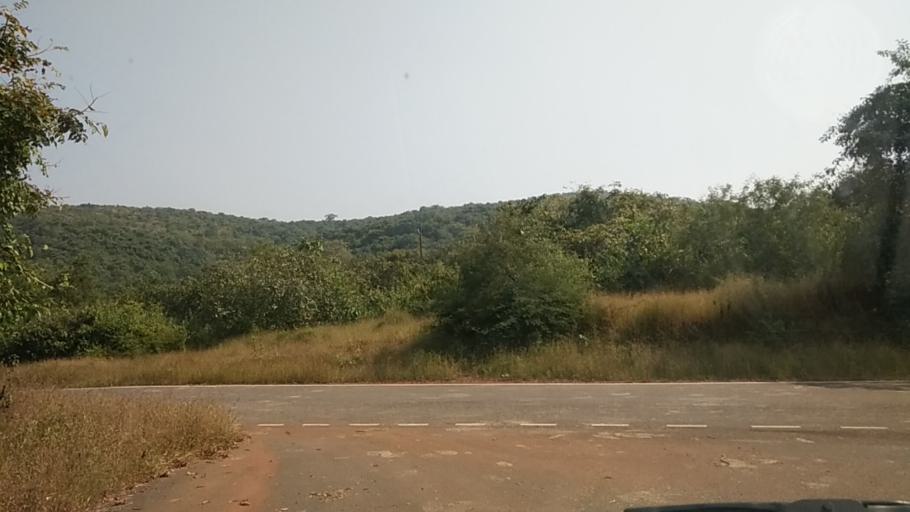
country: IN
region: Goa
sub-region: South Goa
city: Cuncolim
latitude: 15.1337
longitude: 73.9835
